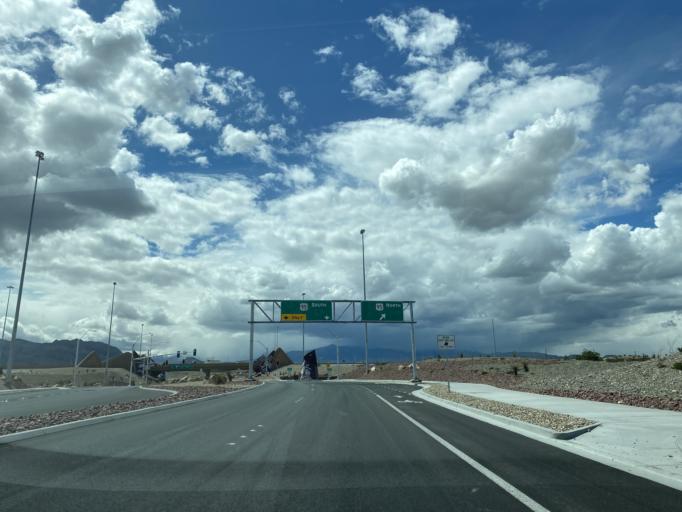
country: US
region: Nevada
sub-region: Clark County
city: Summerlin South
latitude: 36.3269
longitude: -115.3087
